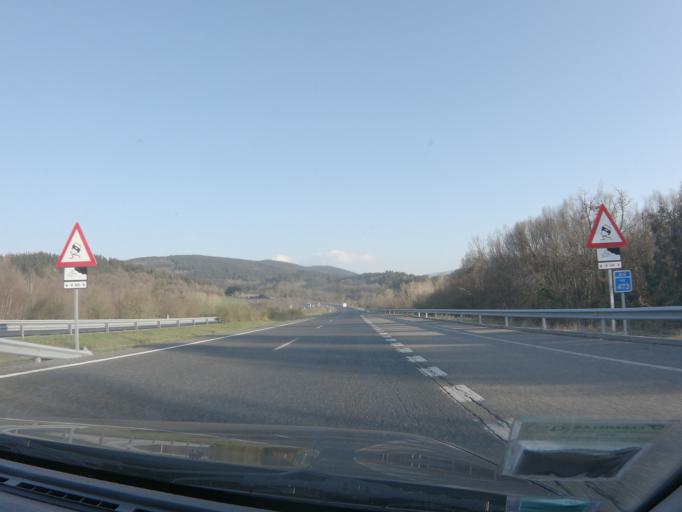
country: ES
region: Galicia
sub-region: Provincia de Lugo
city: Lancara
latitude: 42.9149
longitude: -7.3367
